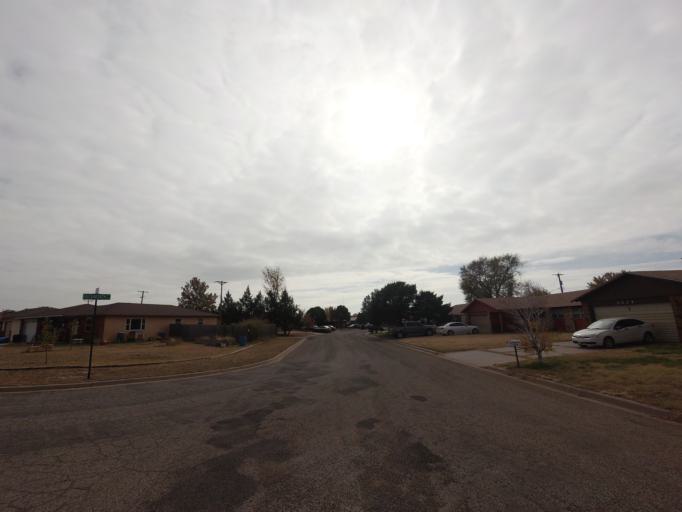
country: US
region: New Mexico
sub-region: Curry County
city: Clovis
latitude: 34.4312
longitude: -103.2171
